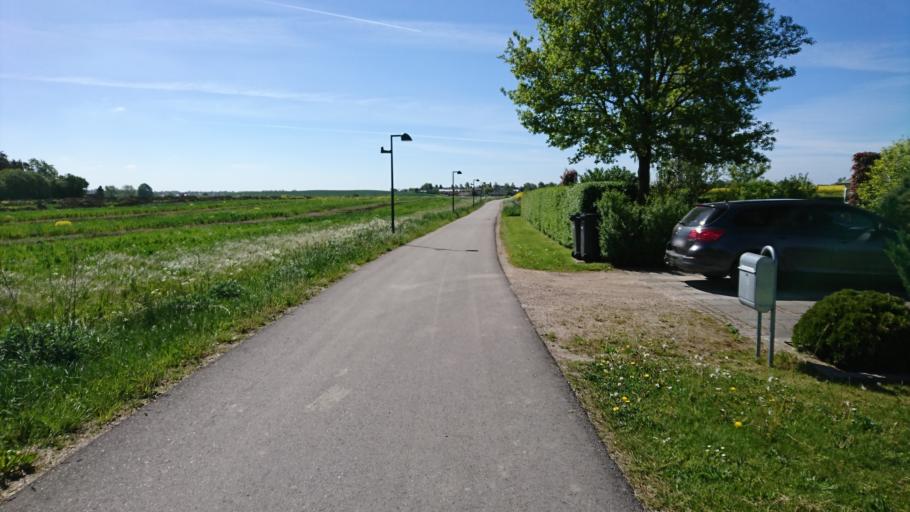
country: DK
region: Capital Region
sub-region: Egedal Kommune
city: Olstykke
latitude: 55.8071
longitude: 12.1154
